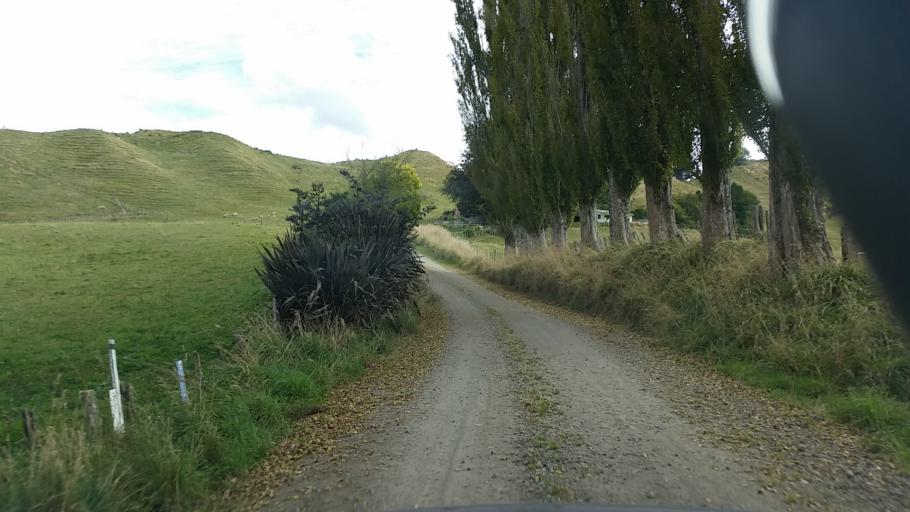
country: NZ
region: Taranaki
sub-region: South Taranaki District
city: Eltham
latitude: -39.2590
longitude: 174.5566
